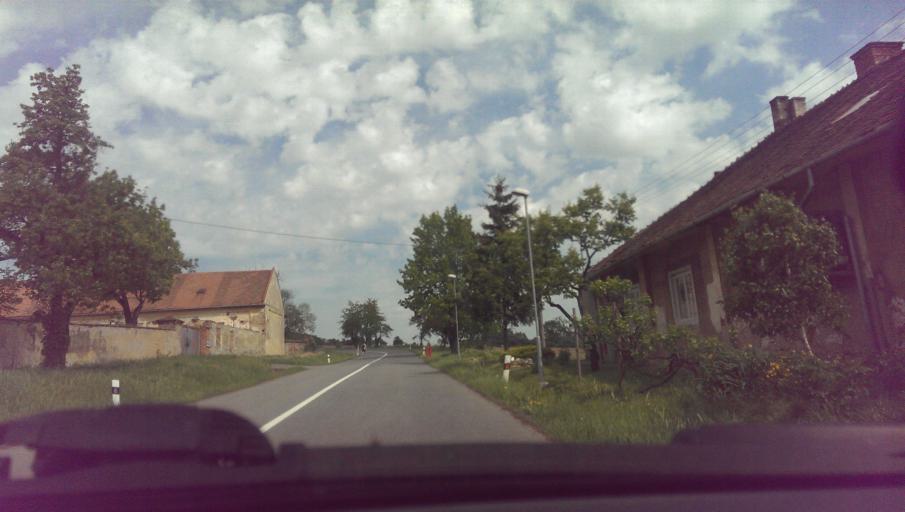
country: CZ
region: Zlin
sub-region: Okres Zlin
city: Otrokovice
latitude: 49.2362
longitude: 17.5384
